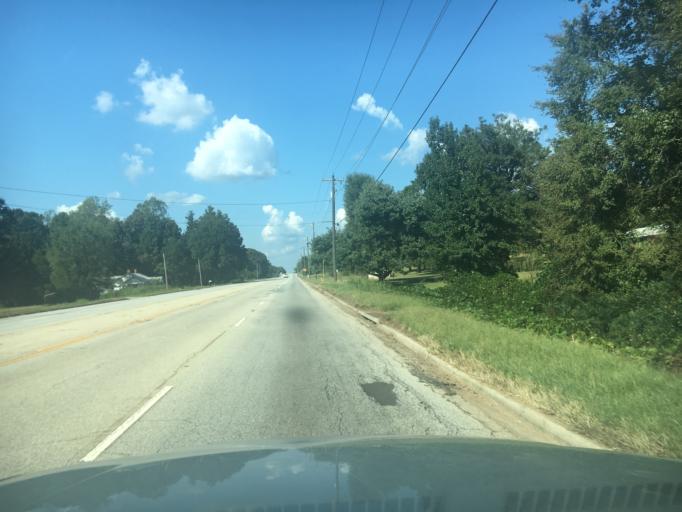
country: US
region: South Carolina
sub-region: Greenwood County
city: Ware Shoals
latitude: 34.3399
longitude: -82.2217
